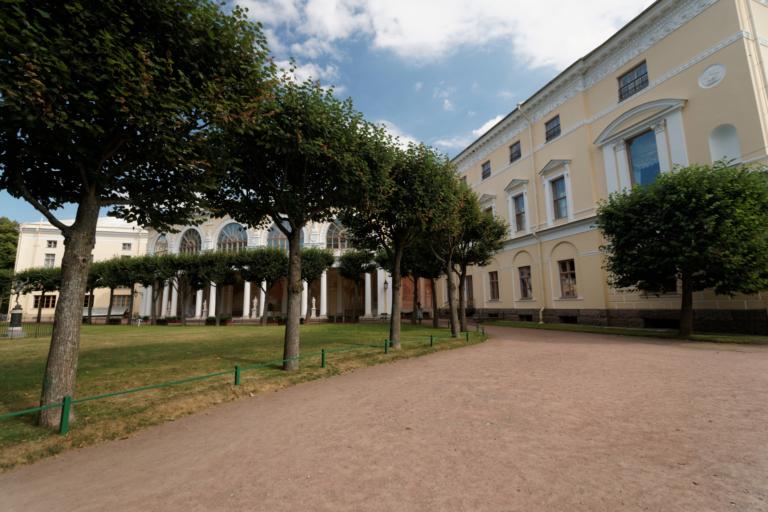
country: RU
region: St.-Petersburg
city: Tyarlevo
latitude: 59.6860
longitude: 30.4521
